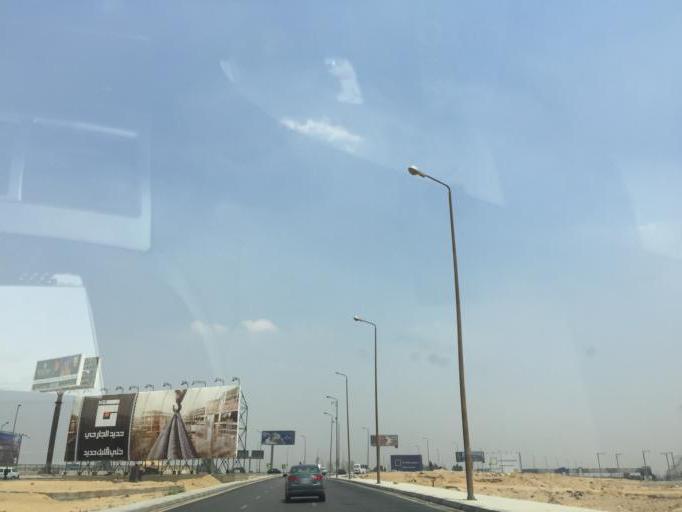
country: EG
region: Muhafazat al Qahirah
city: Cairo
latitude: 30.0180
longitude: 31.4025
